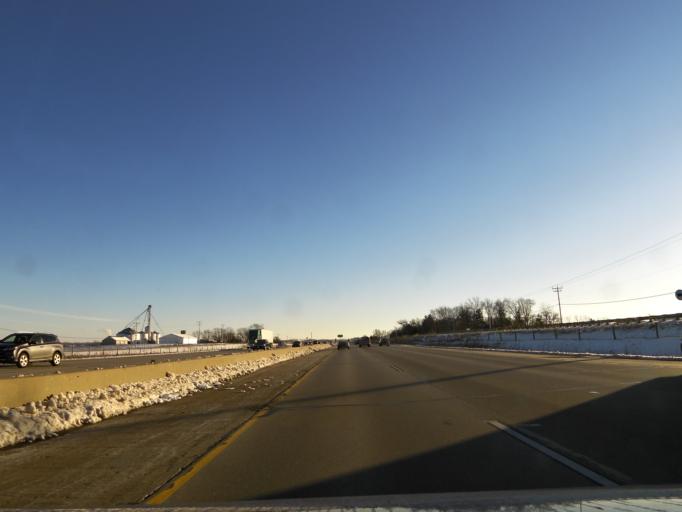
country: US
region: Wisconsin
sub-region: Kenosha County
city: Somers
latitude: 42.6330
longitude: -87.9527
